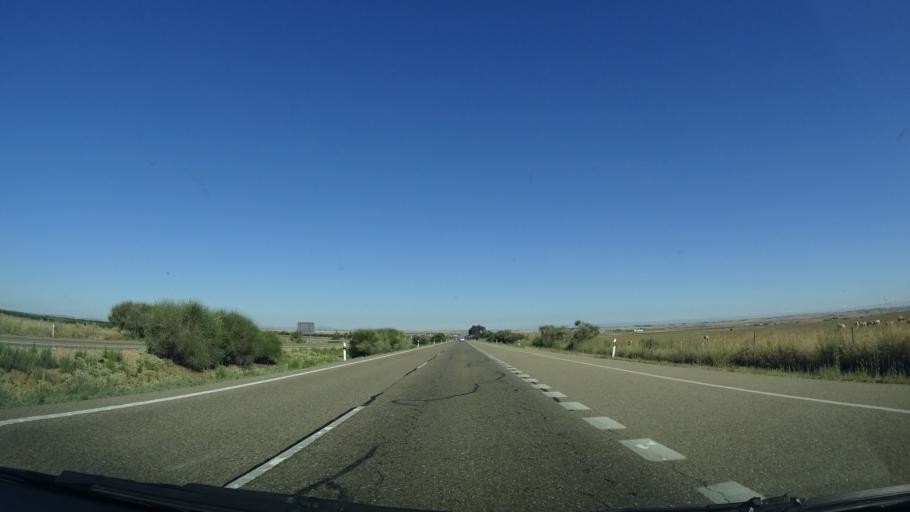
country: ES
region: Castille and Leon
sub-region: Provincia de Zamora
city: Villalpando
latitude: 41.8300
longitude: -5.3806
